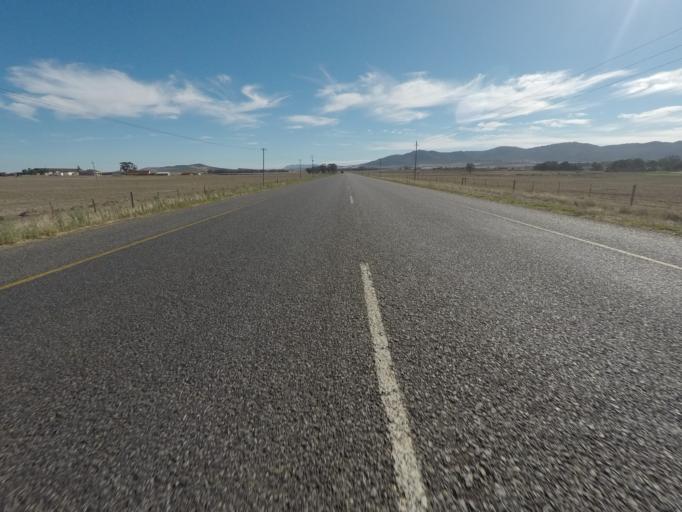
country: ZA
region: Western Cape
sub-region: West Coast District Municipality
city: Malmesbury
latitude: -33.6376
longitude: 18.7182
